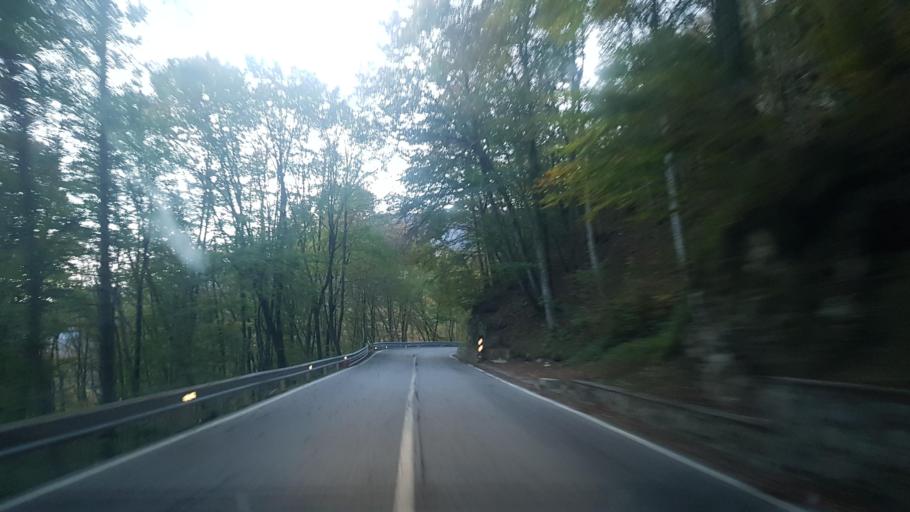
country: IT
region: Friuli Venezia Giulia
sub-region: Provincia di Udine
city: Chiaulis
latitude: 46.3791
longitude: 12.9606
